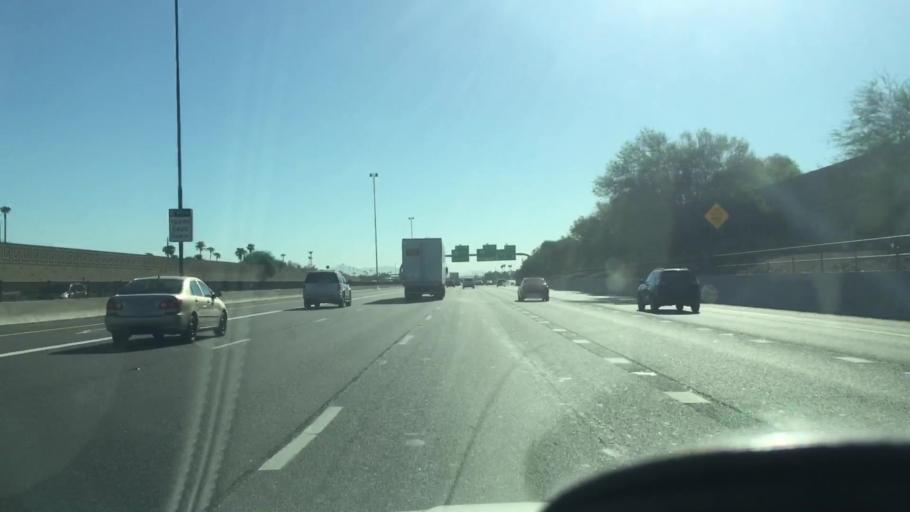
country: US
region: Arizona
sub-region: Maricopa County
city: Tempe
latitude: 33.3868
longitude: -111.9184
